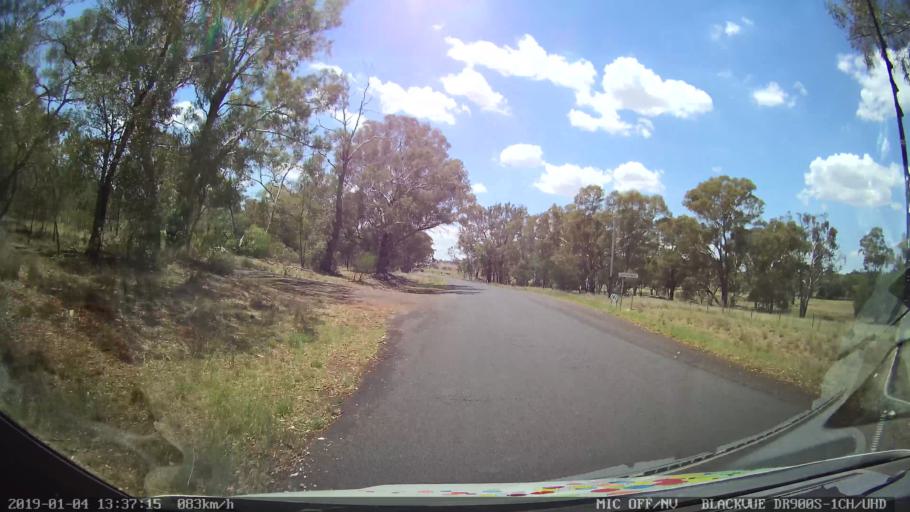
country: AU
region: New South Wales
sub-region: Dubbo Municipality
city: Dubbo
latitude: -32.5521
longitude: 148.5419
